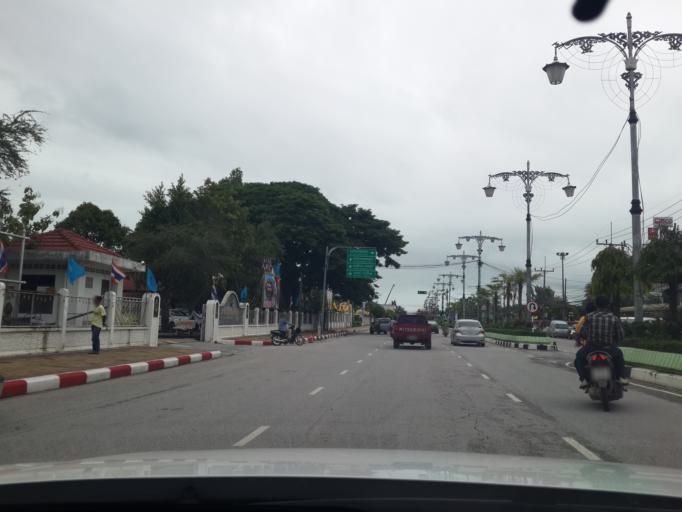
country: TH
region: Pattani
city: Pattani
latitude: 6.8672
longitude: 101.2510
